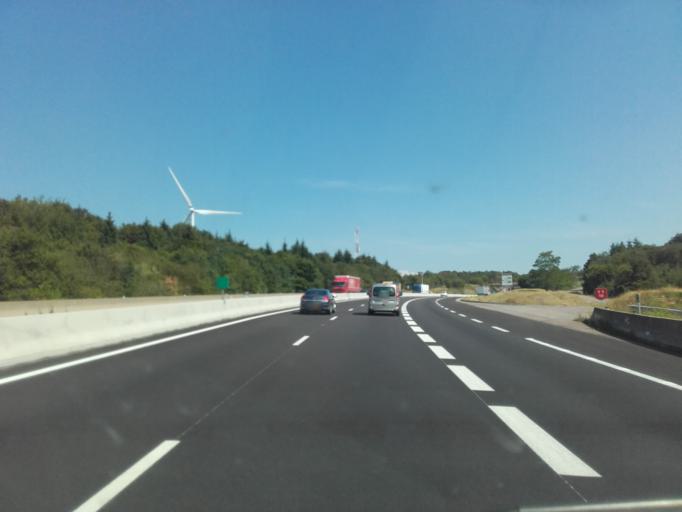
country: FR
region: Bourgogne
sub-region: Departement de la Cote-d'Or
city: Savigny-les-Beaune
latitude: 47.1021
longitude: 4.7375
